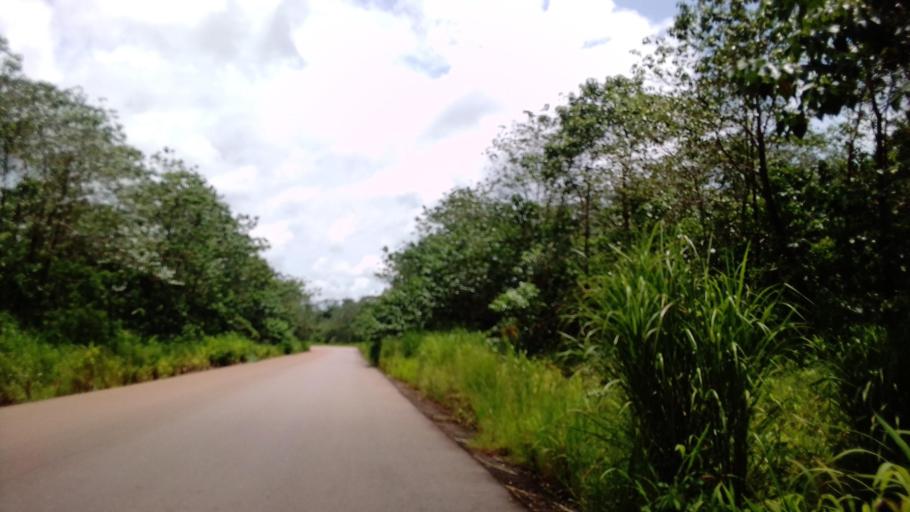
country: SL
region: Northern Province
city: Makeni
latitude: 9.0853
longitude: -12.1894
